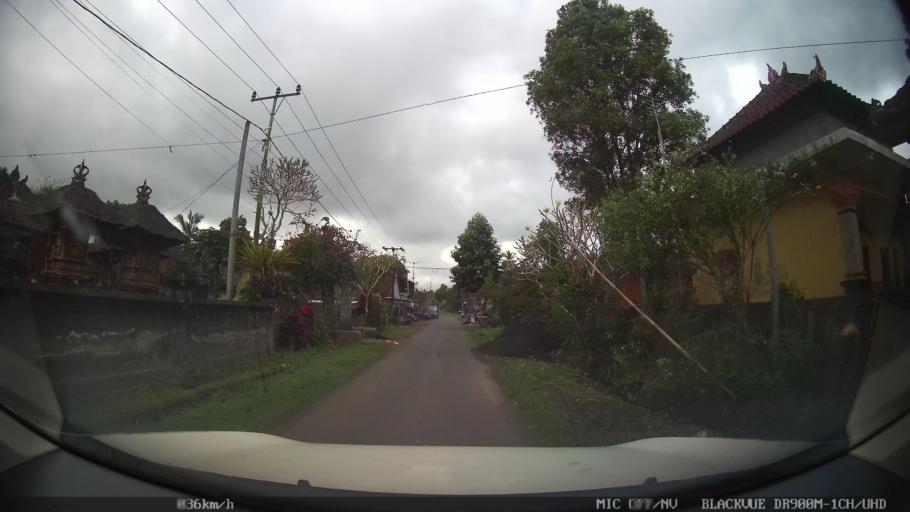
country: ID
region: Bali
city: Banjar Wangsian
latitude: -8.4462
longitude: 115.4241
